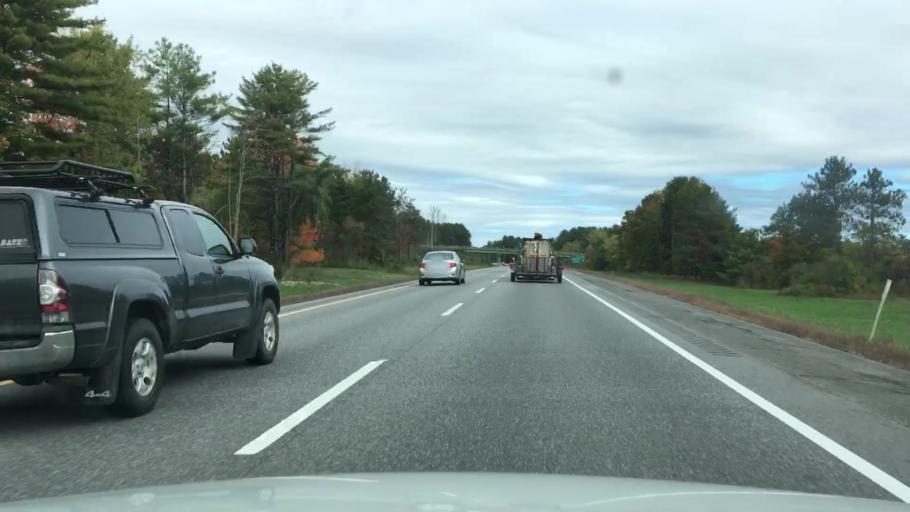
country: US
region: Maine
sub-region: Kennebec County
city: Sidney
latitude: 44.4502
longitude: -69.7180
